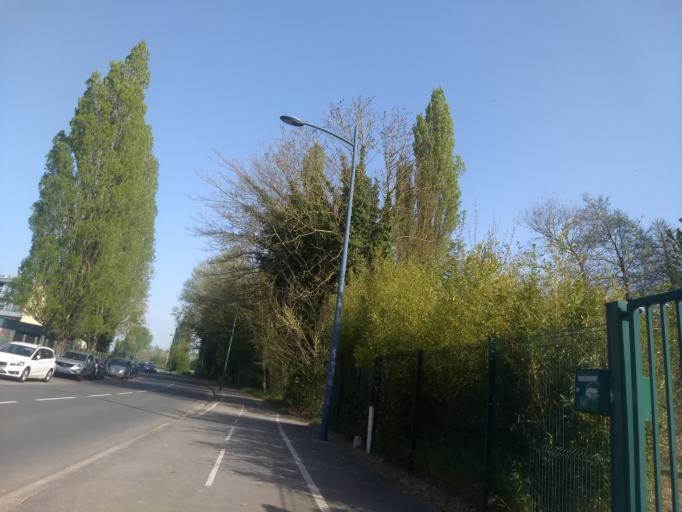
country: FR
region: Nord-Pas-de-Calais
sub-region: Departement du Pas-de-Calais
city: Anzin-Saint-Aubin
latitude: 50.3011
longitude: 2.7521
